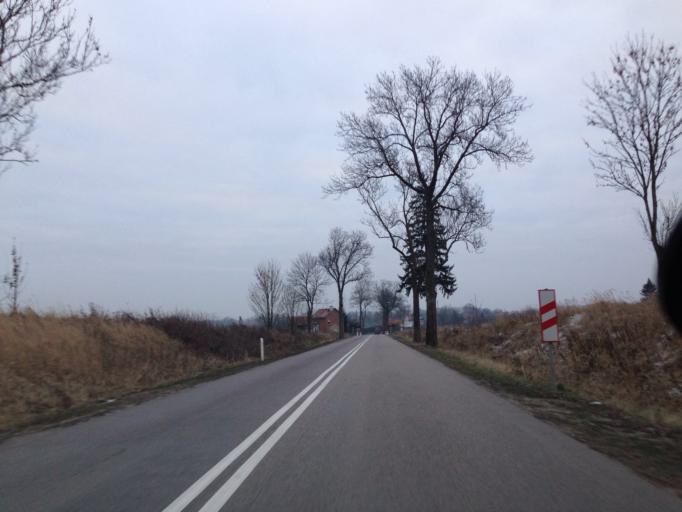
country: PL
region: Warmian-Masurian Voivodeship
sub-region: Powiat ketrzynski
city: Ketrzyn
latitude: 54.0720
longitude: 21.3133
